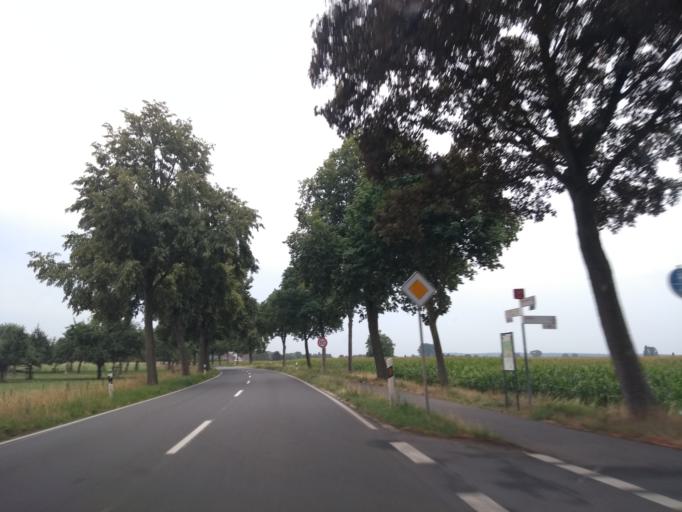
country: DE
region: North Rhine-Westphalia
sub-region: Regierungsbezirk Dusseldorf
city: Kleve
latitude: 51.8379
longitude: 6.0930
